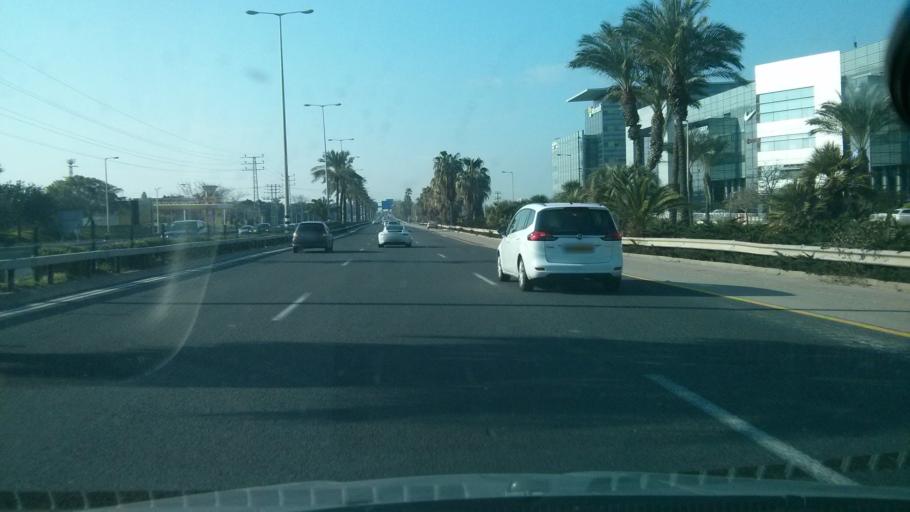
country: IL
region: Tel Aviv
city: Herzliyya
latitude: 32.1595
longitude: 34.8106
